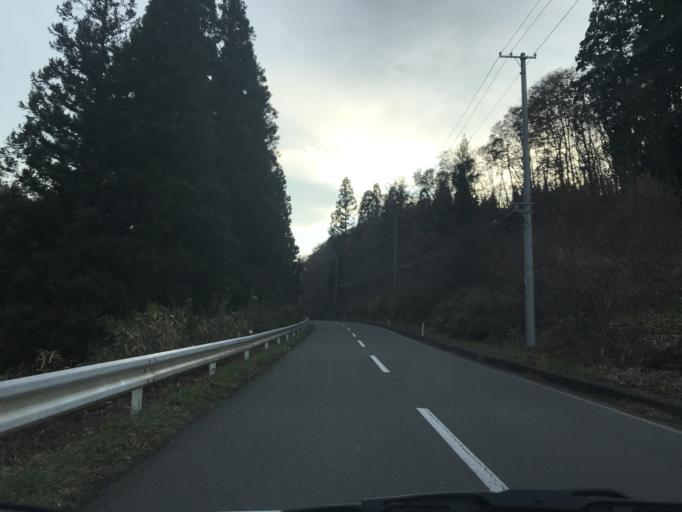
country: JP
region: Iwate
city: Ichinoseki
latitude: 38.9610
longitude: 141.0568
